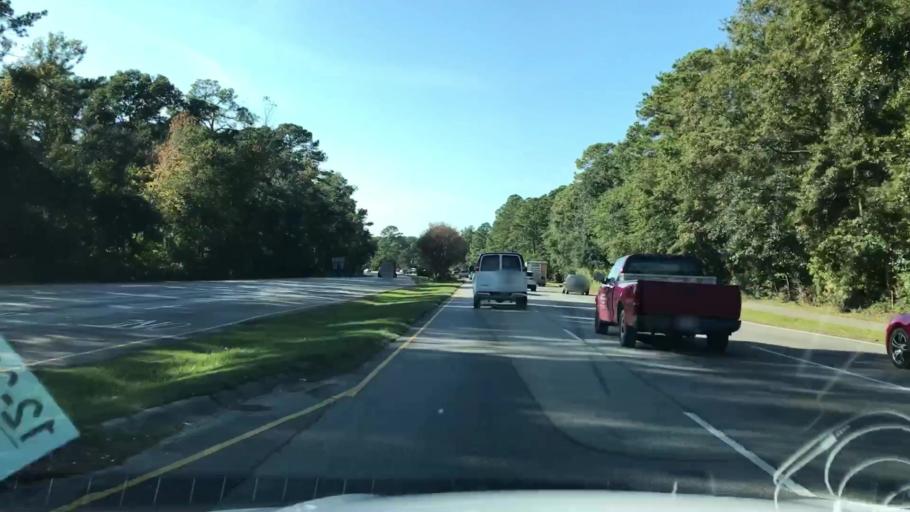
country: US
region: South Carolina
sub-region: Beaufort County
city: Hilton Head Island
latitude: 32.2172
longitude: -80.7125
